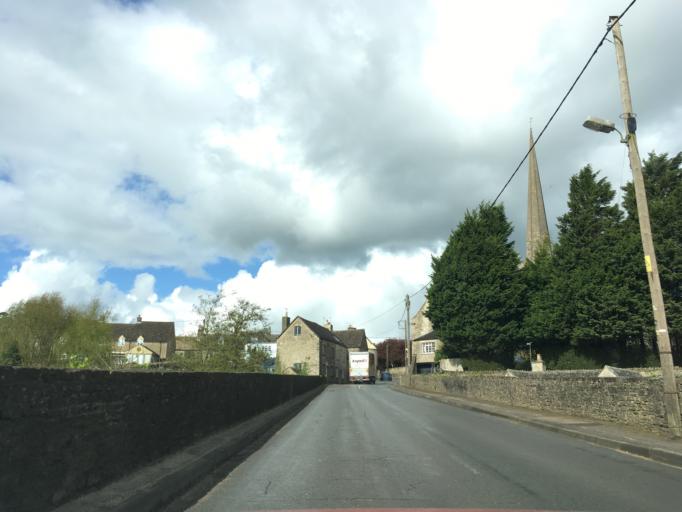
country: GB
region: England
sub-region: Gloucestershire
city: Tetbury
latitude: 51.6346
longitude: -2.1613
